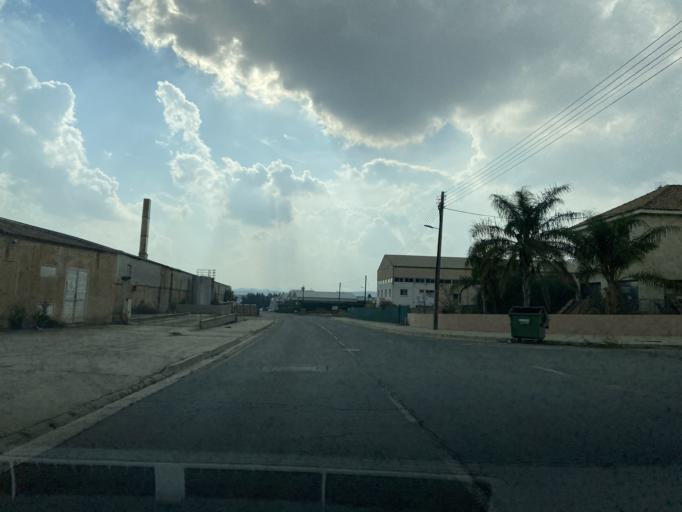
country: CY
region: Lefkosia
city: Dali
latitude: 35.0575
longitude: 33.3940
